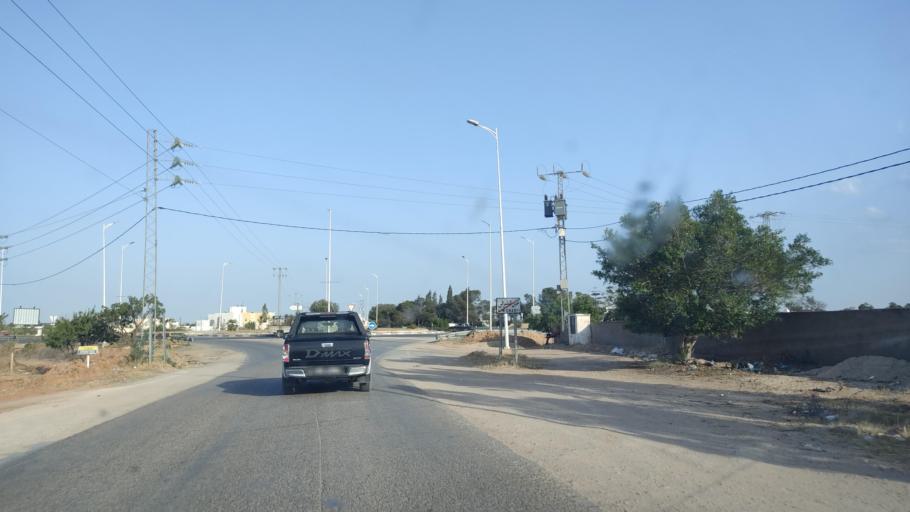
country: TN
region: Safaqis
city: Sfax
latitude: 34.7974
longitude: 10.6783
